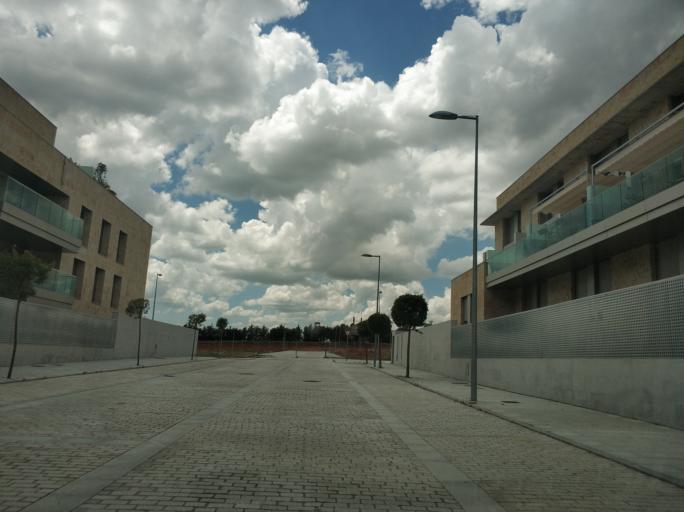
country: ES
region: Castille and Leon
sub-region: Provincia de Salamanca
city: Aldeatejada
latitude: 40.9460
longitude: -5.6821
